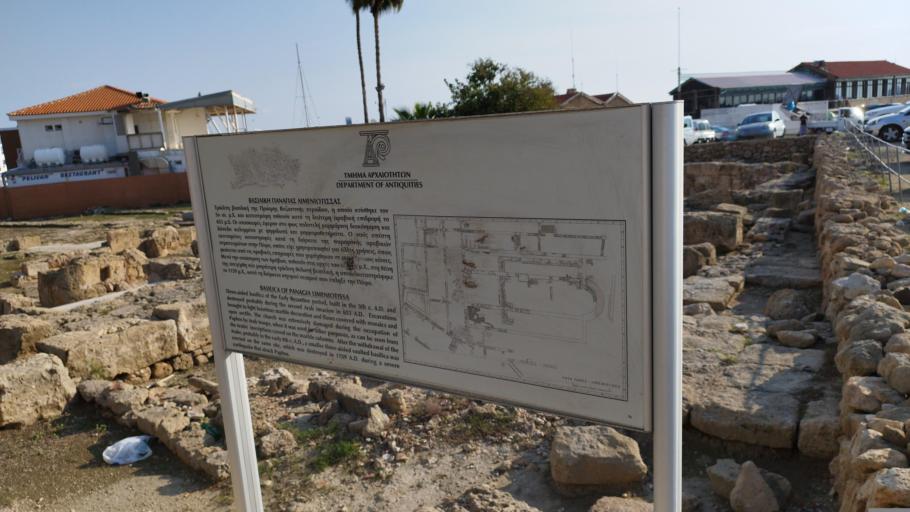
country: CY
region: Pafos
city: Paphos
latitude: 34.7560
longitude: 32.4076
